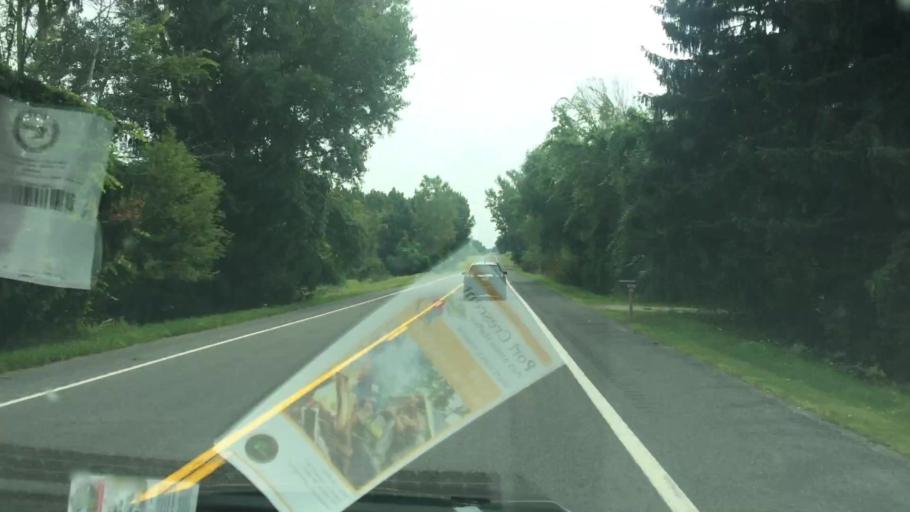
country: US
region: Michigan
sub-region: Huron County
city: Harbor Beach
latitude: 44.0188
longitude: -82.8053
